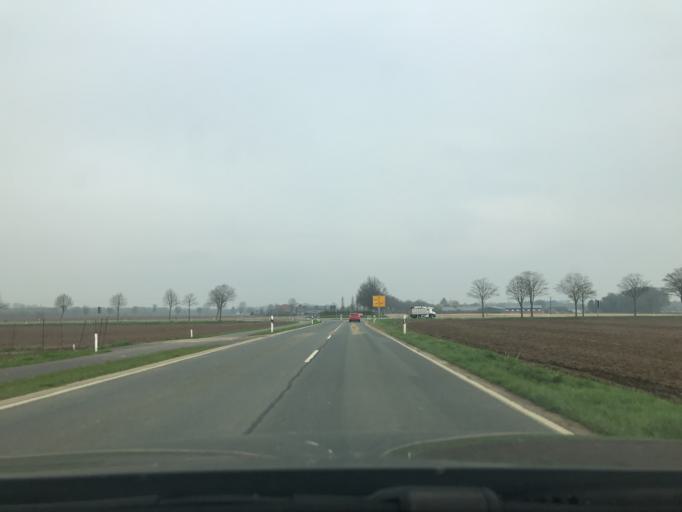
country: DE
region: North Rhine-Westphalia
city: Geldern
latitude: 51.4869
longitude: 6.3204
